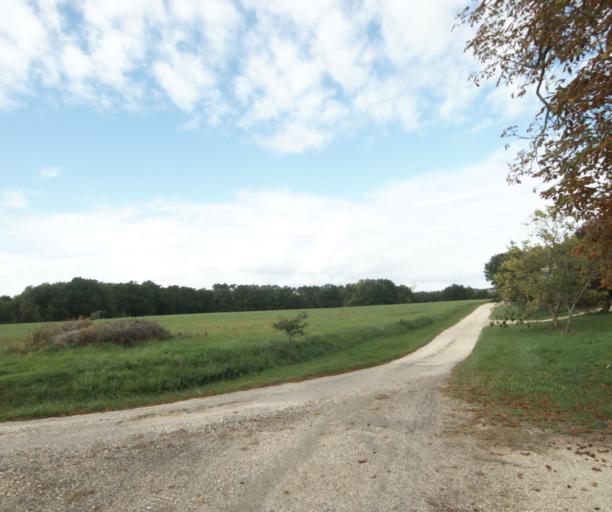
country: FR
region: Midi-Pyrenees
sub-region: Departement du Gers
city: Montreal
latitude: 43.9282
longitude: 0.1340
